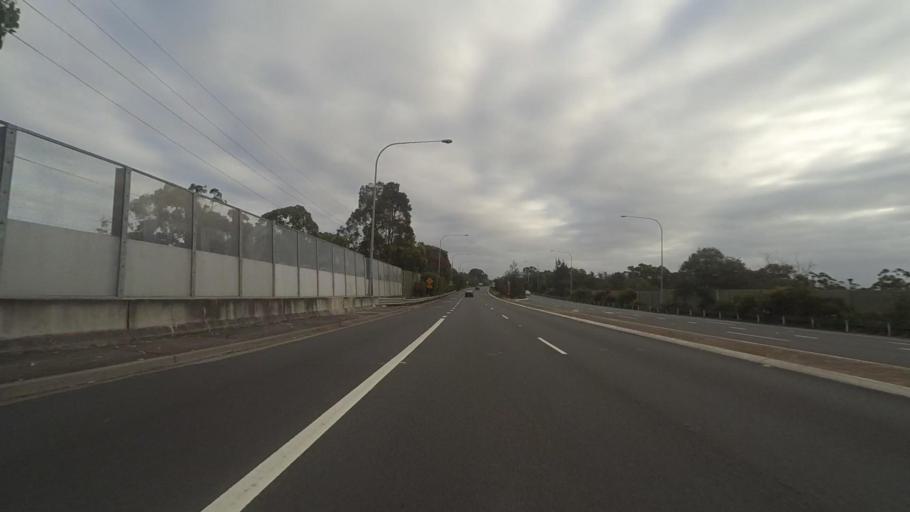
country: AU
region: New South Wales
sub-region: Sutherland Shire
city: Menai
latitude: -34.0235
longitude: 151.0079
